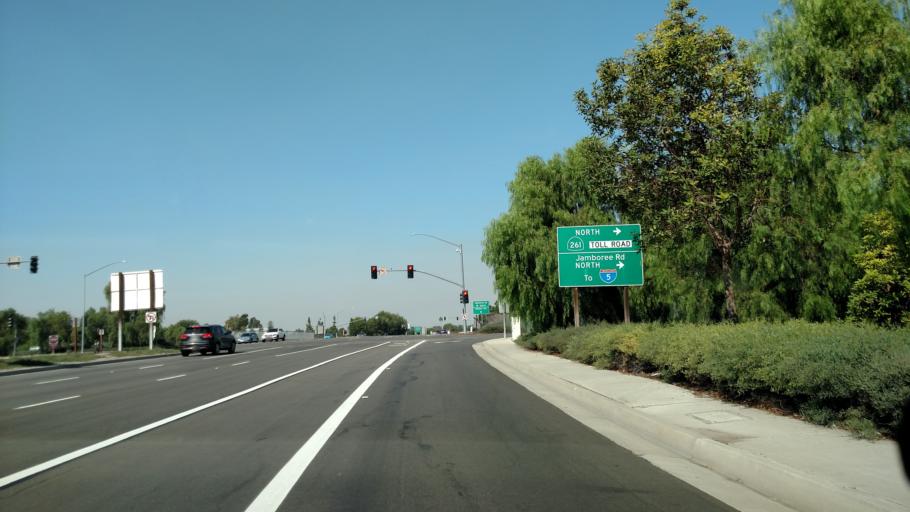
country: US
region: California
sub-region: Orange County
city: Tustin
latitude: 33.7113
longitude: -117.7992
